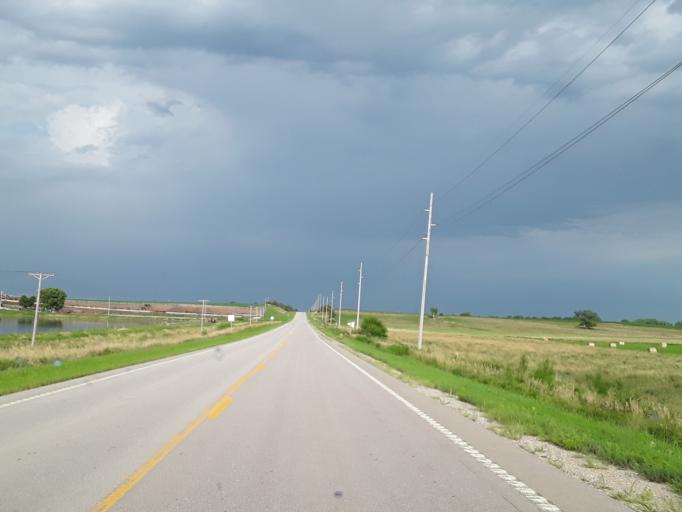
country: US
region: Nebraska
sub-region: Saunders County
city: Ashland
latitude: 41.0887
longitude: -96.4201
